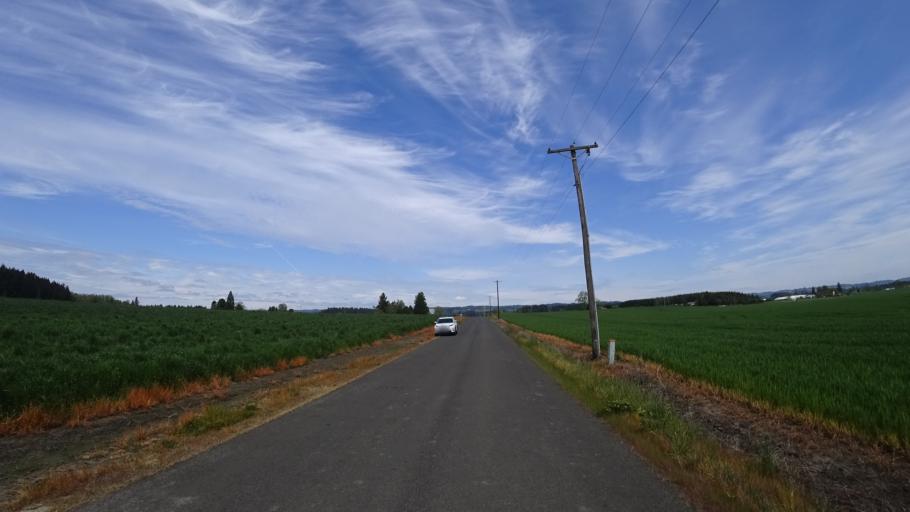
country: US
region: Oregon
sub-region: Washington County
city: North Plains
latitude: 45.5761
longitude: -122.9387
